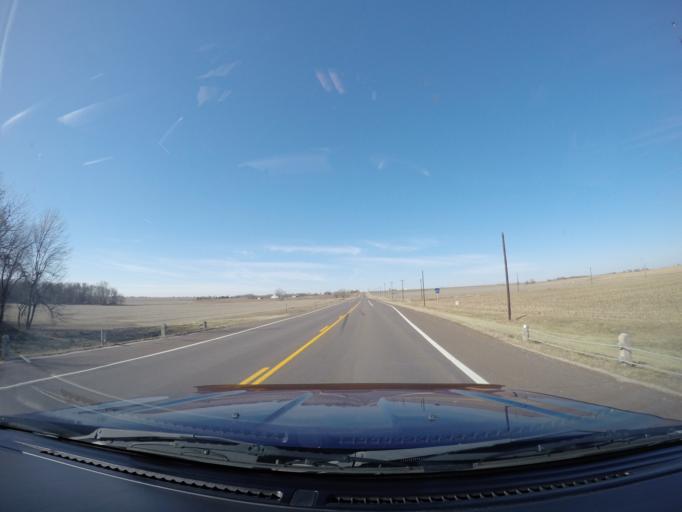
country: US
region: Kansas
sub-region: Clay County
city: Clay Center
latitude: 39.3810
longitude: -97.0705
